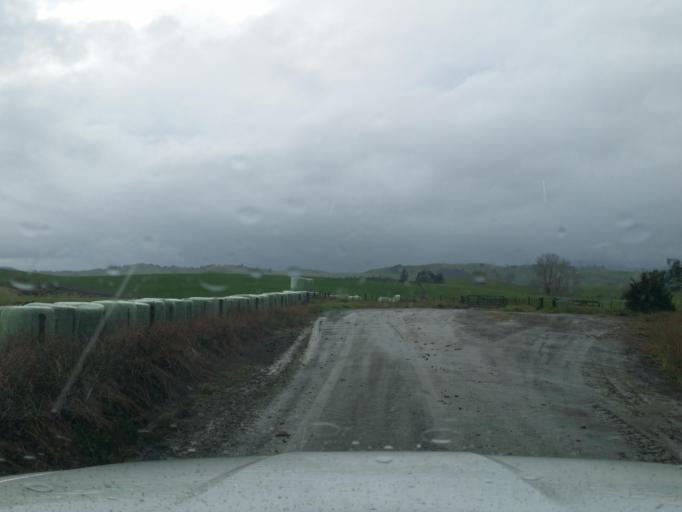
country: NZ
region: Northland
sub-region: Kaipara District
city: Dargaville
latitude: -35.9466
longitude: 174.0656
